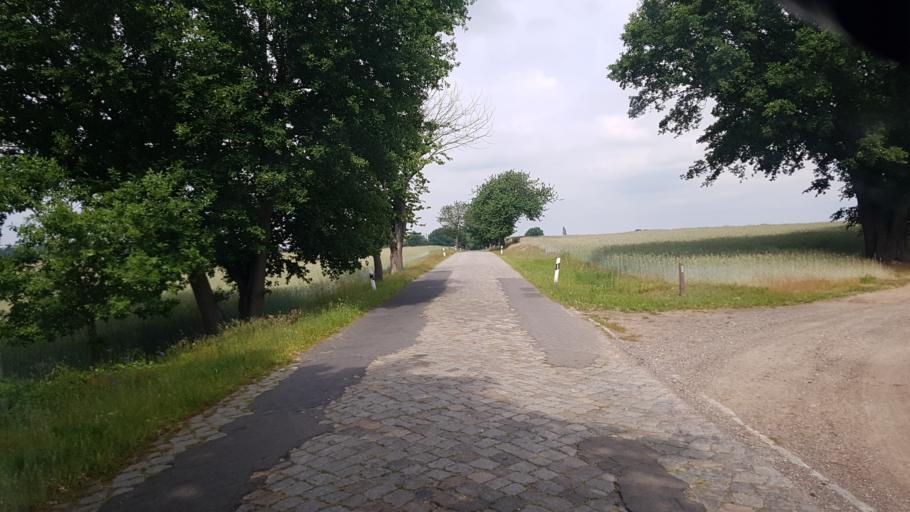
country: DE
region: Brandenburg
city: Lebusa
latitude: 51.8044
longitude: 13.4500
